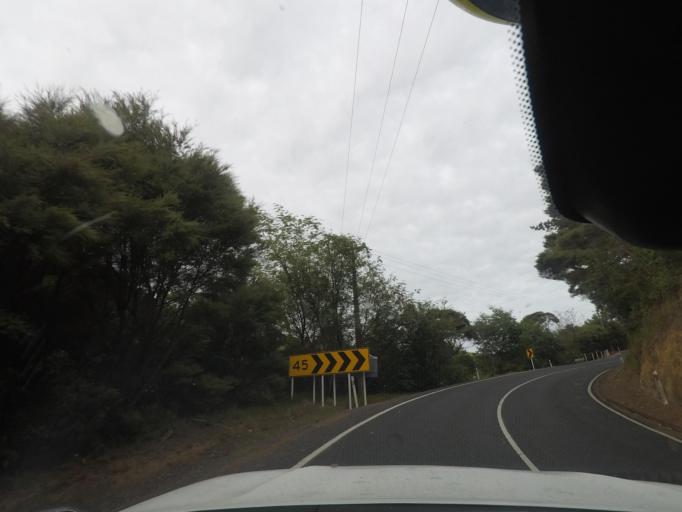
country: NZ
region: Auckland
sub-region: Auckland
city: Parakai
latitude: -36.5219
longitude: 174.2755
